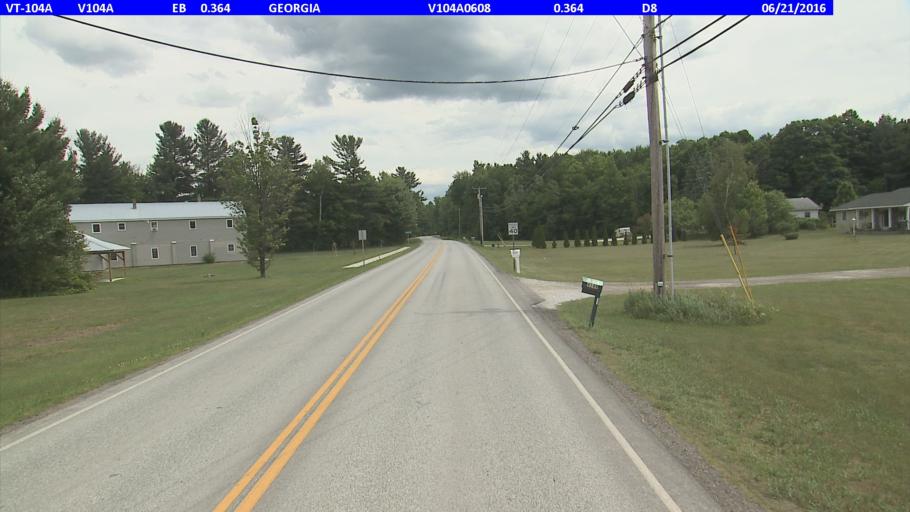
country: US
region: Vermont
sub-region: Chittenden County
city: Milton
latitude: 44.6913
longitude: -73.1023
